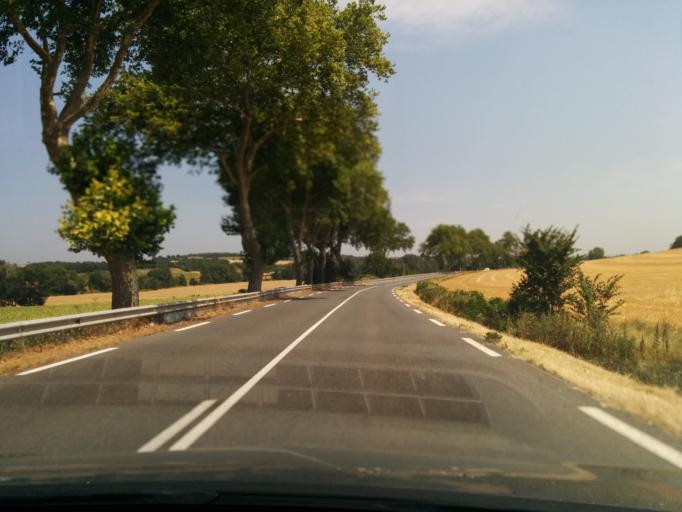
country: FR
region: Languedoc-Roussillon
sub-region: Departement de l'Aude
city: Villepinte
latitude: 43.2887
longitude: 2.0639
